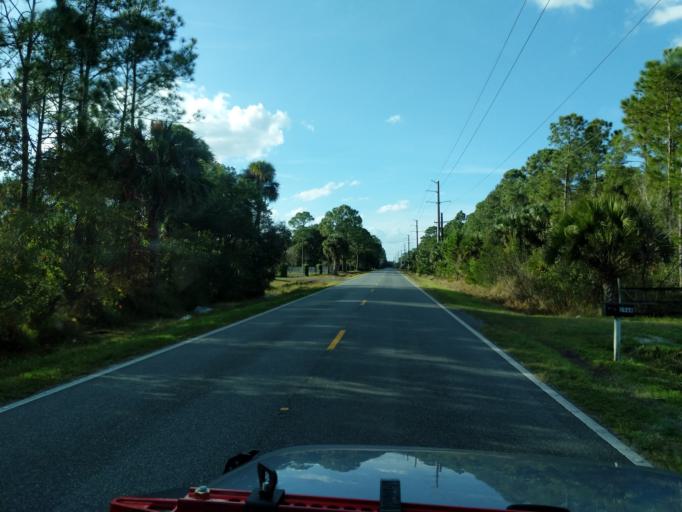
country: US
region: Florida
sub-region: Seminole County
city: Geneva
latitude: 28.7742
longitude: -81.1562
